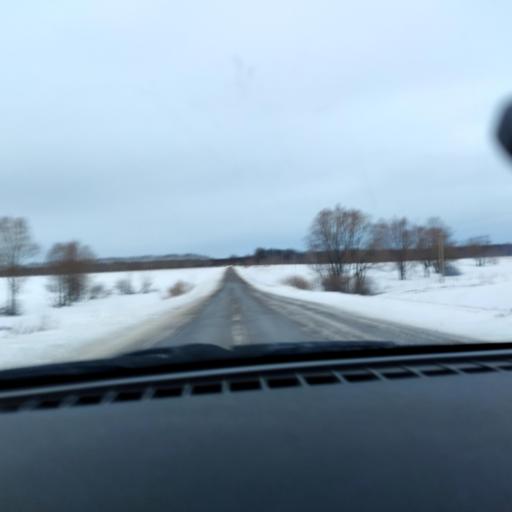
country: RU
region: Bashkortostan
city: Iglino
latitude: 54.7790
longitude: 56.5380
